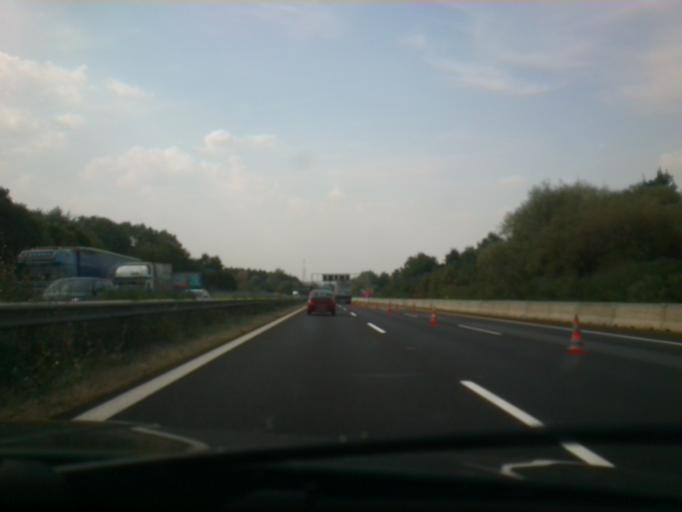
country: CZ
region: Central Bohemia
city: Velke Popovice
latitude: 49.9539
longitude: 14.6390
